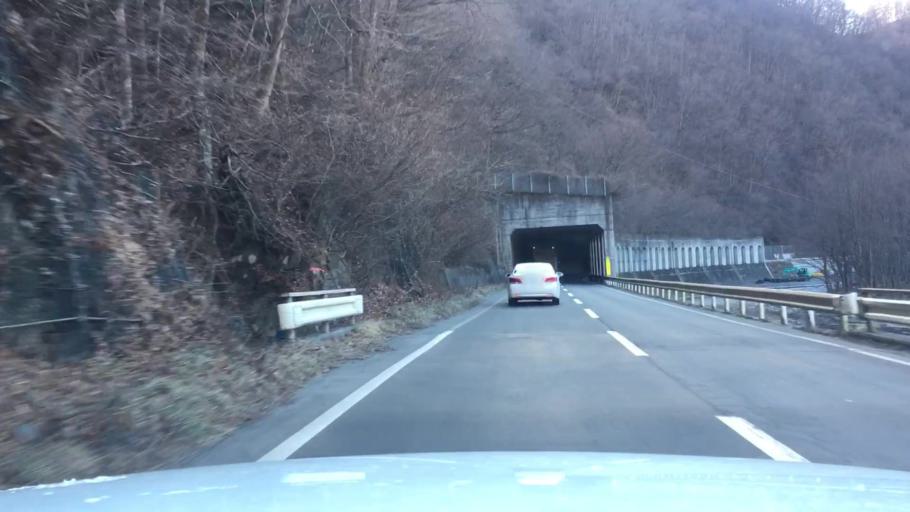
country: JP
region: Iwate
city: Miyako
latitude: 39.6070
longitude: 141.6530
